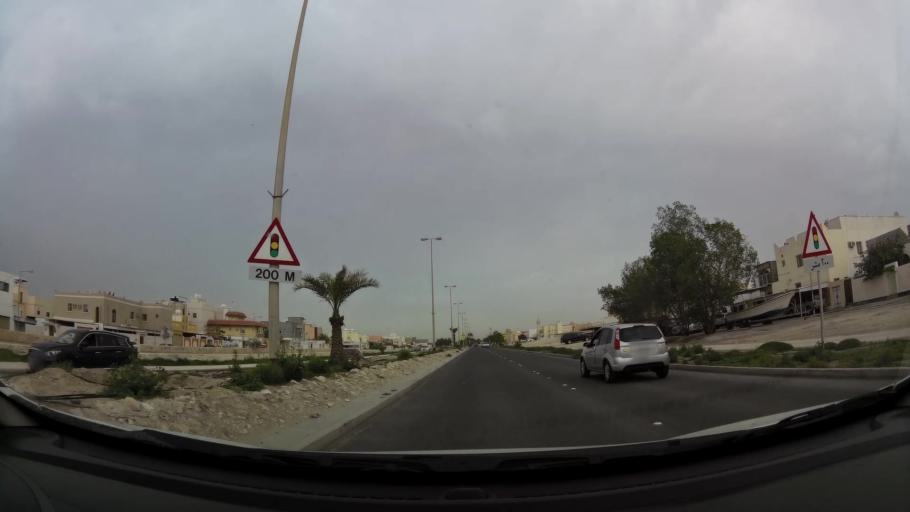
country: BH
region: Central Governorate
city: Dar Kulayb
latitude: 26.0638
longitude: 50.5078
